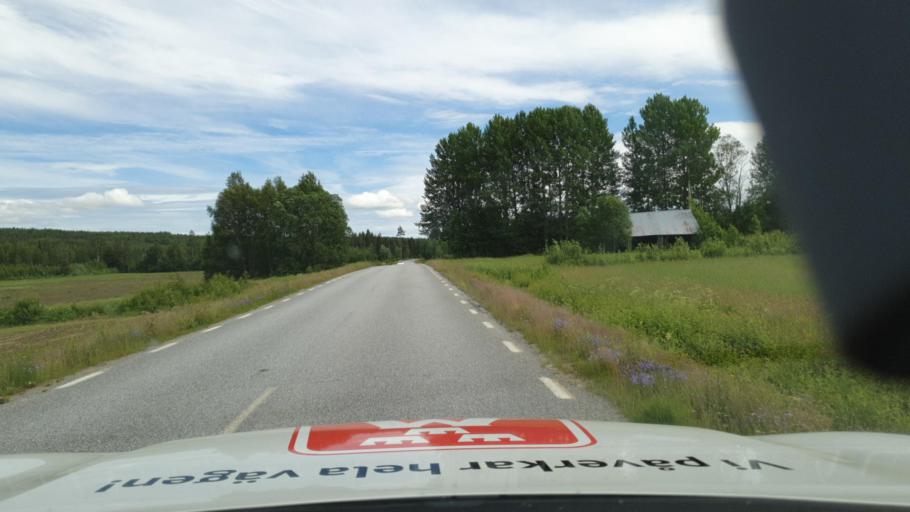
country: SE
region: Vaesterbotten
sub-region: Skelleftea Kommun
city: Viken
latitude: 64.5163
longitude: 20.9869
